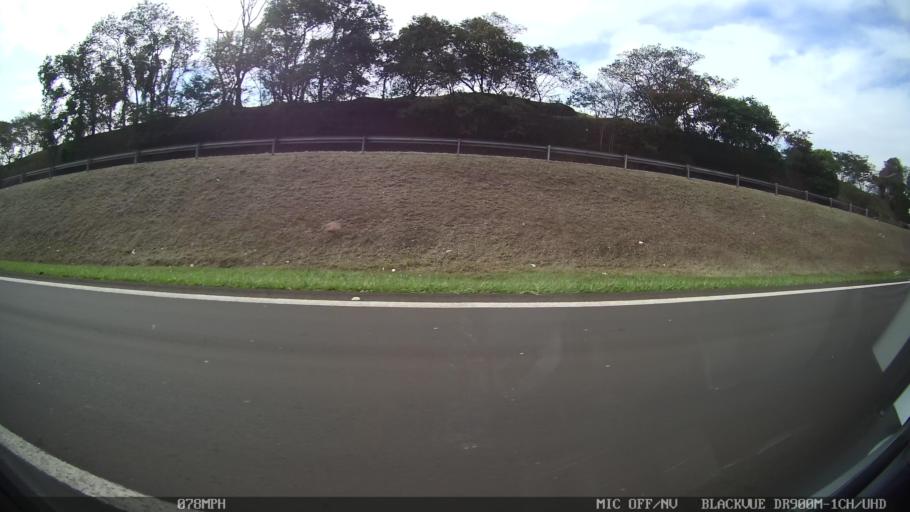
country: BR
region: Sao Paulo
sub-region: Matao
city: Matao
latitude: -21.5819
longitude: -48.4510
